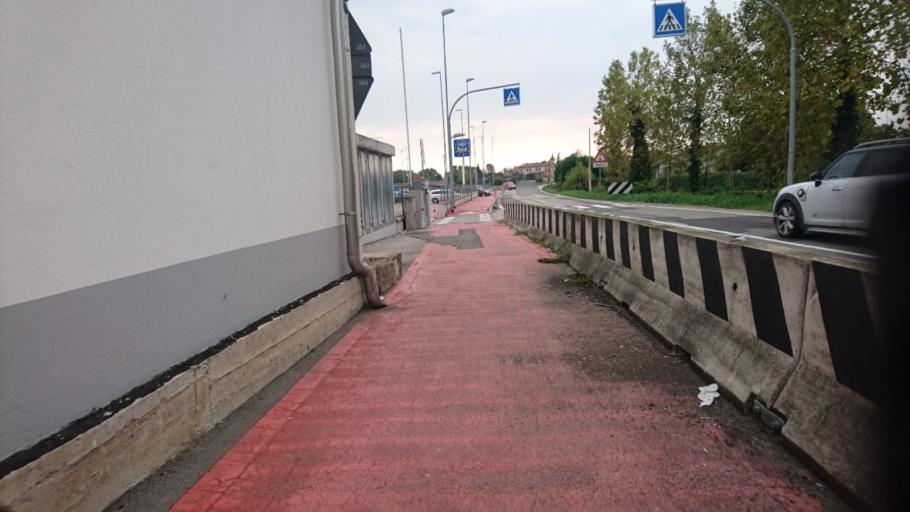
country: IT
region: Veneto
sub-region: Provincia di Verona
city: San Martino Buon Albergo
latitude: 45.4060
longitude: 11.0853
